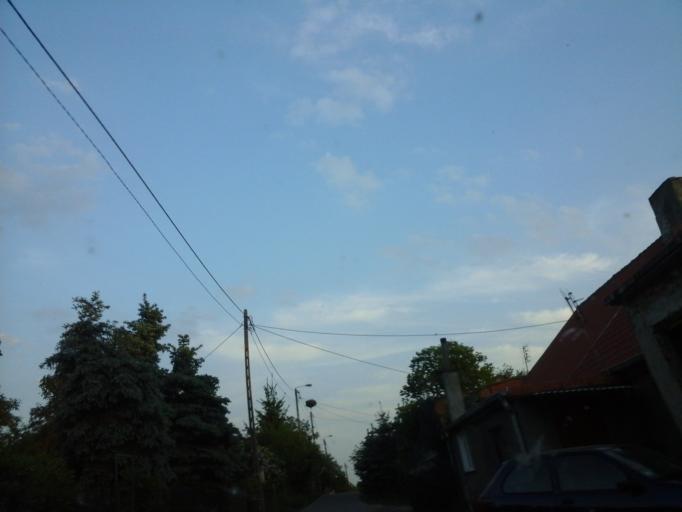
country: PL
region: West Pomeranian Voivodeship
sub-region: Powiat choszczenski
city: Choszczno
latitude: 53.1886
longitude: 15.4159
